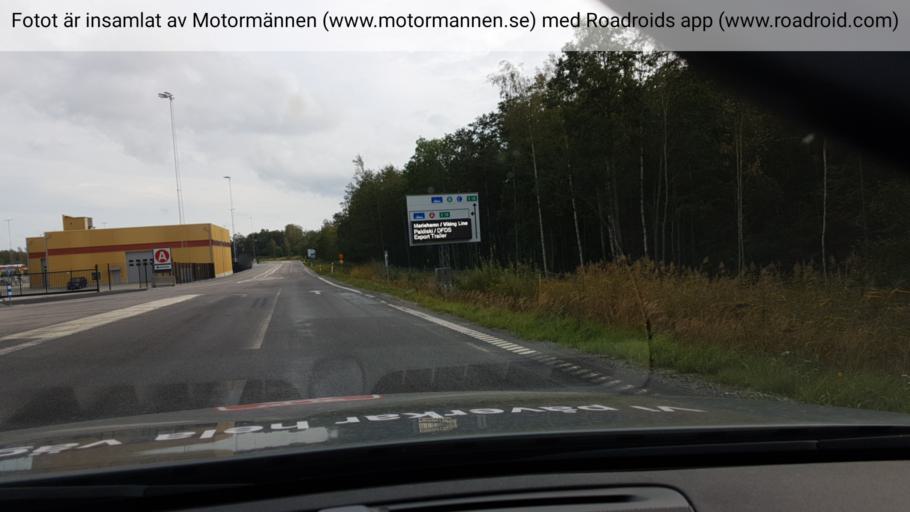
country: SE
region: Stockholm
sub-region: Norrtalje Kommun
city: Bjorko
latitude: 59.7222
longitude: 19.0575
